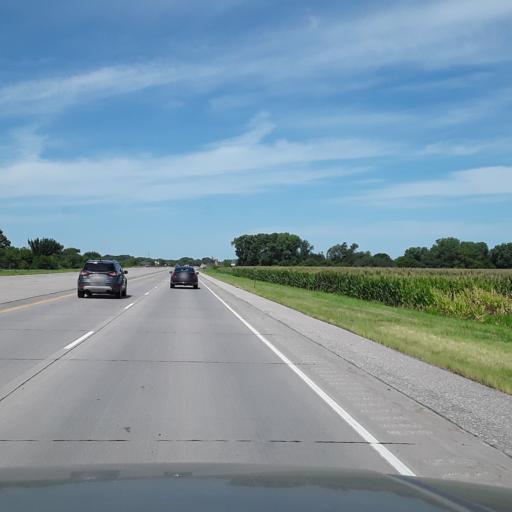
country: US
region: Nebraska
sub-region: Lancaster County
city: Lincoln
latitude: 40.8797
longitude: -96.7703
